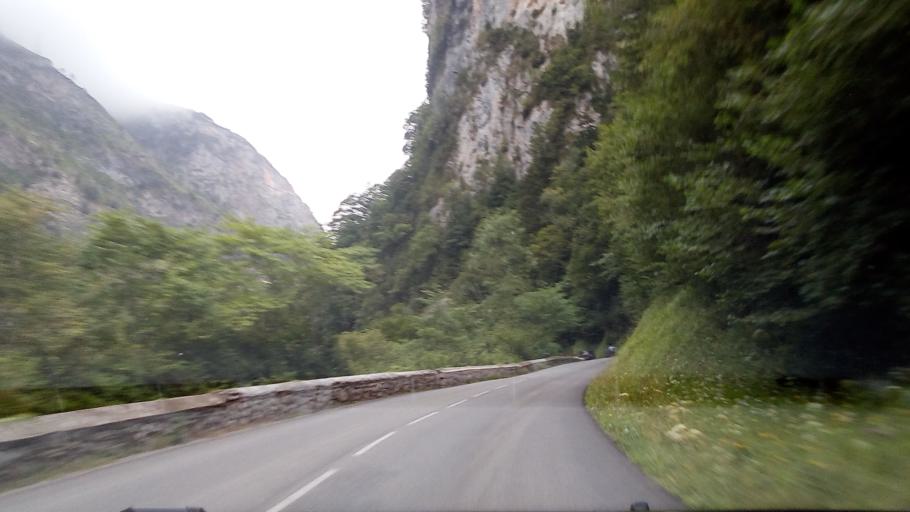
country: FR
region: Aquitaine
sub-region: Departement des Pyrenees-Atlantiques
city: Laruns
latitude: 42.9665
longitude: -0.4395
